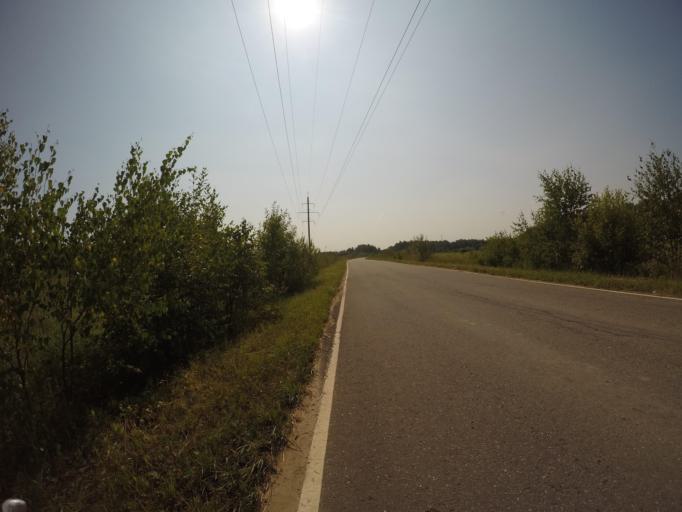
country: RU
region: Moskovskaya
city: Rechitsy
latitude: 55.6260
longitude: 38.5205
